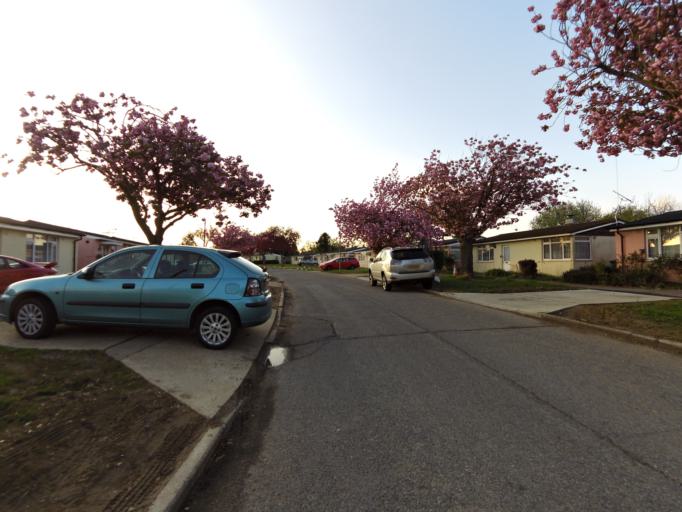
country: GB
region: England
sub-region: Suffolk
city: Ipswich
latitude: 52.0732
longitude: 1.1877
